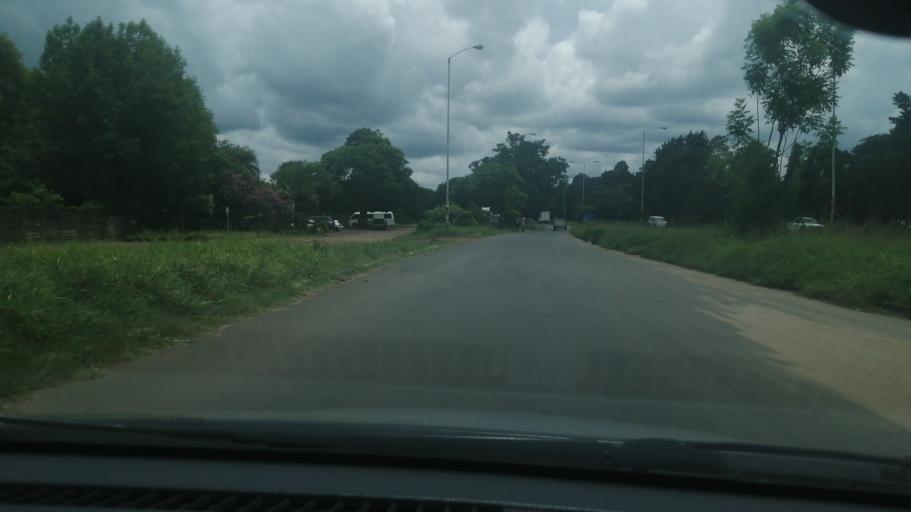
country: ZW
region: Harare
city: Harare
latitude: -17.8302
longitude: 31.0708
